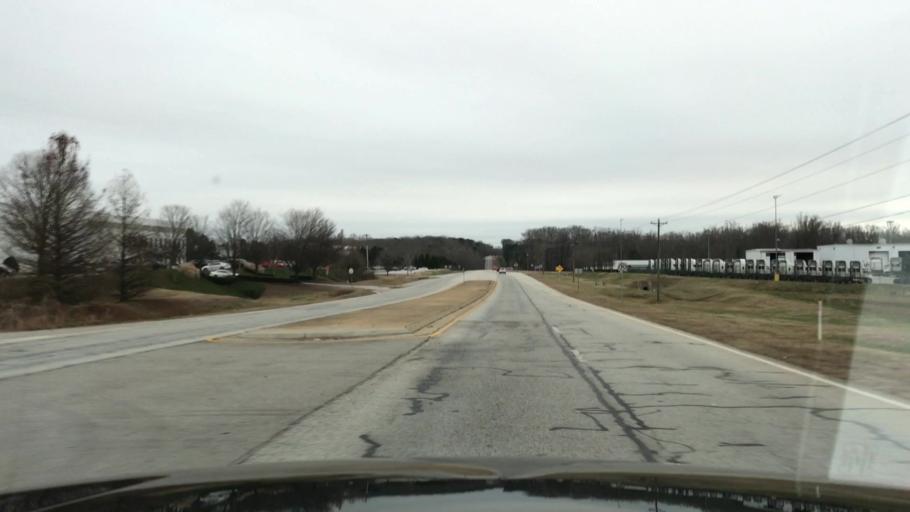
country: US
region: Georgia
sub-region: Walton County
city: Monroe
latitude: 33.8097
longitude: -83.6773
